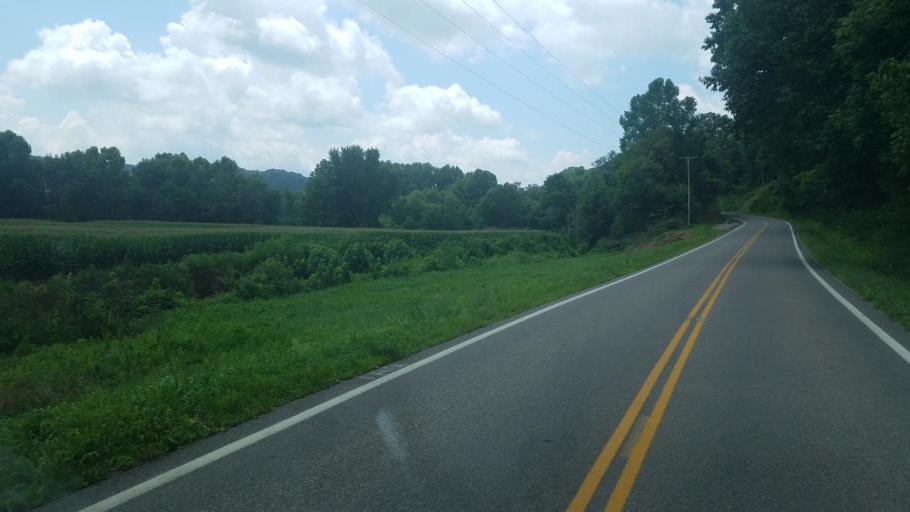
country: US
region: Ohio
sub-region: Ross County
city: Chillicothe
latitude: 39.2963
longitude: -82.7440
